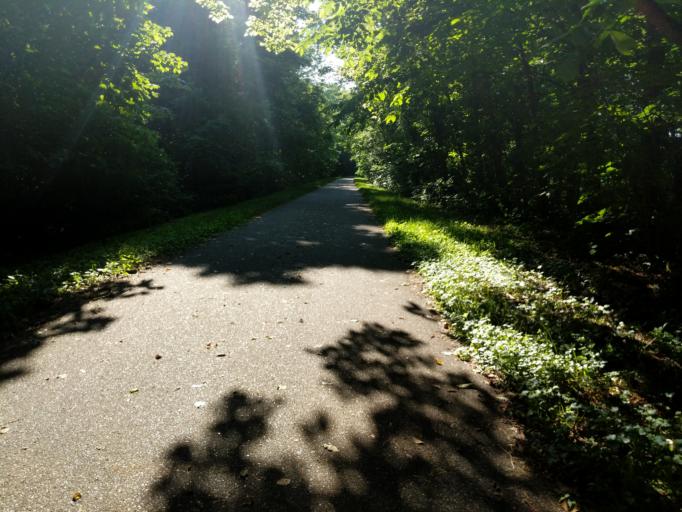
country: US
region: Ohio
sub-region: Athens County
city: Nelsonville
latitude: 39.4278
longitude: -82.2009
